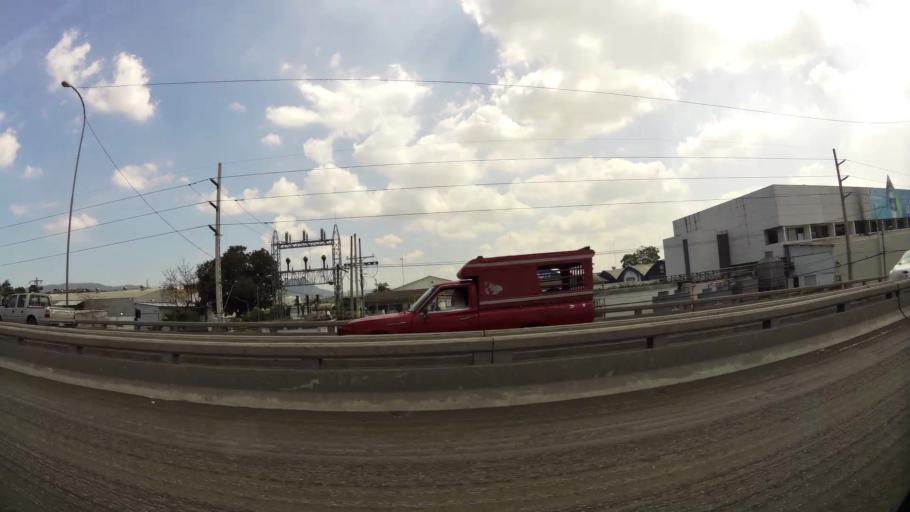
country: EC
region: Guayas
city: Guayaquil
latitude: -2.1221
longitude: -79.9312
